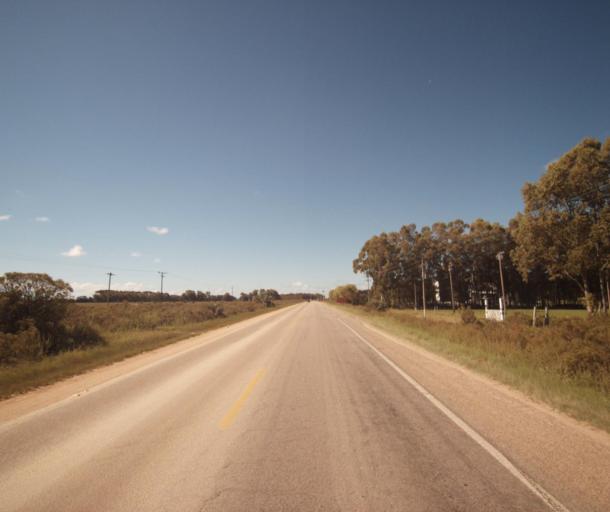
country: BR
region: Rio Grande do Sul
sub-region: Santa Vitoria Do Palmar
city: Santa Vitoria do Palmar
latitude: -33.5638
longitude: -53.3724
